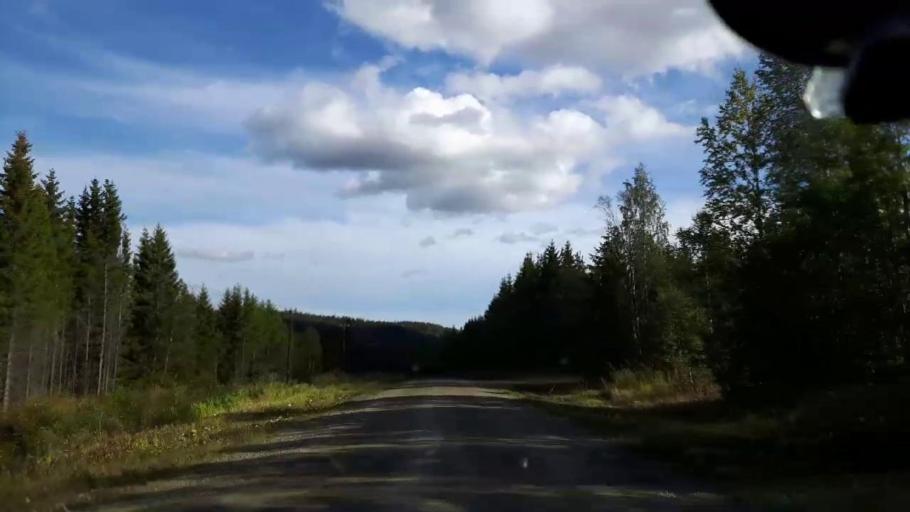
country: SE
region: Jaemtland
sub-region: Ragunda Kommun
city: Hammarstrand
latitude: 63.4253
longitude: 16.0584
